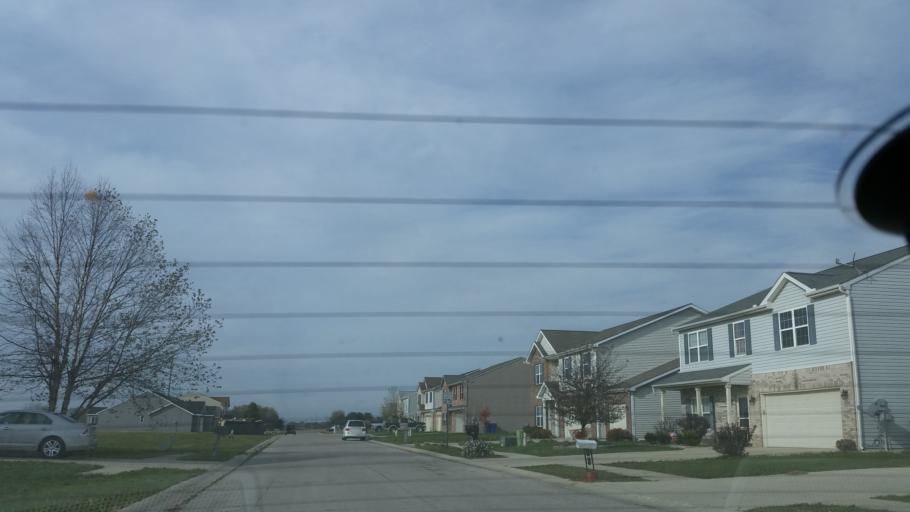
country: US
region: Indiana
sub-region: Howard County
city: Indian Heights
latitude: 40.4452
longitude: -86.1558
